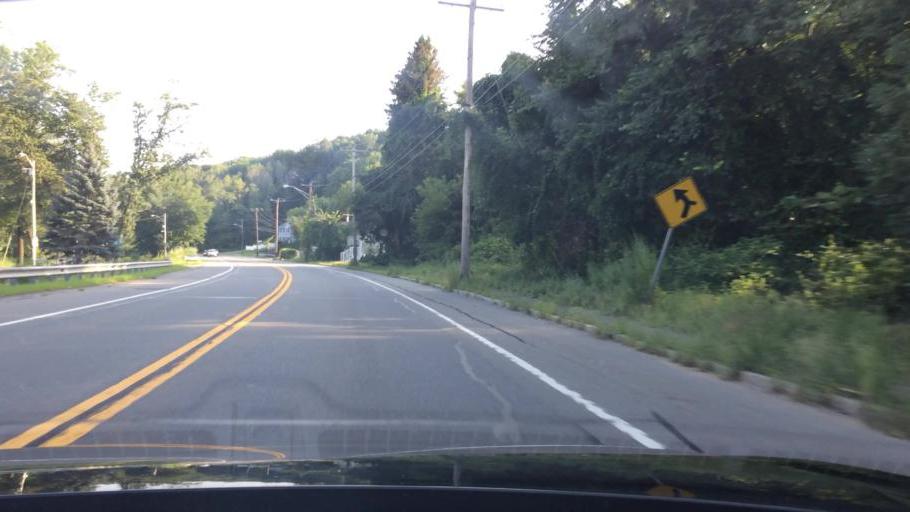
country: US
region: Massachusetts
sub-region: Essex County
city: Haverhill
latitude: 42.7718
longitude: -71.1327
